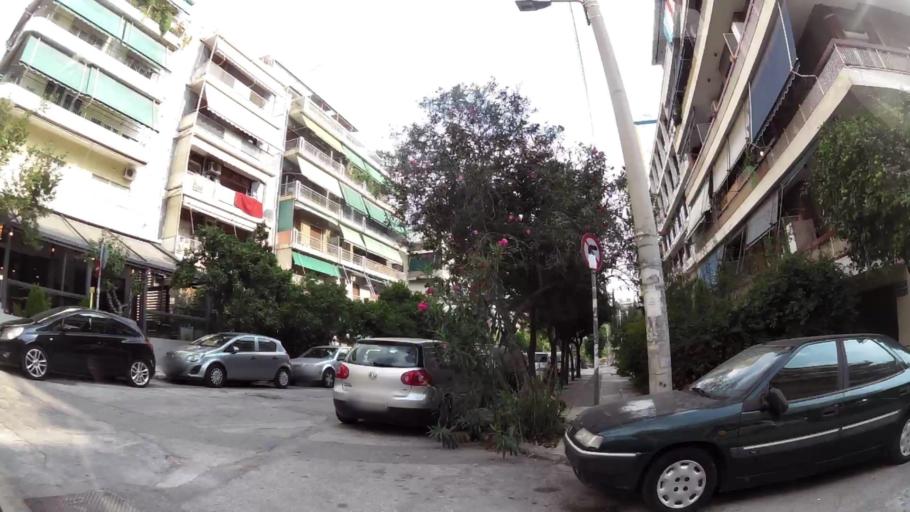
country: GR
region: Attica
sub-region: Nomarchia Athinas
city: Nea Smyrni
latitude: 37.9568
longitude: 23.7148
